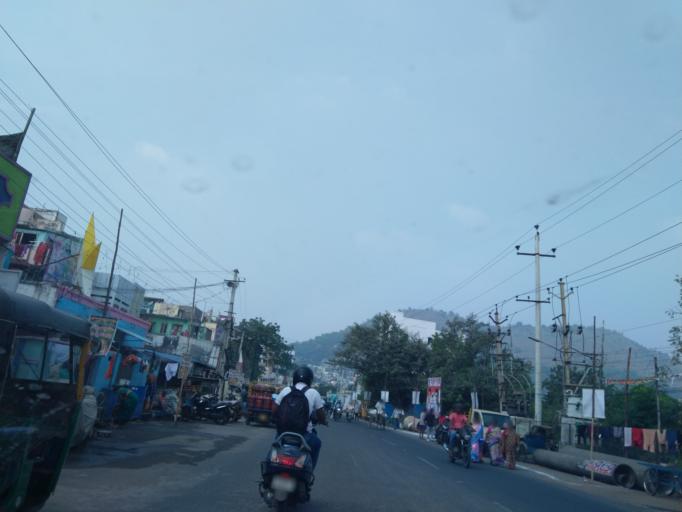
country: IN
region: Andhra Pradesh
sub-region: Krishna
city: Vijayawada
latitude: 16.5303
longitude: 80.6166
